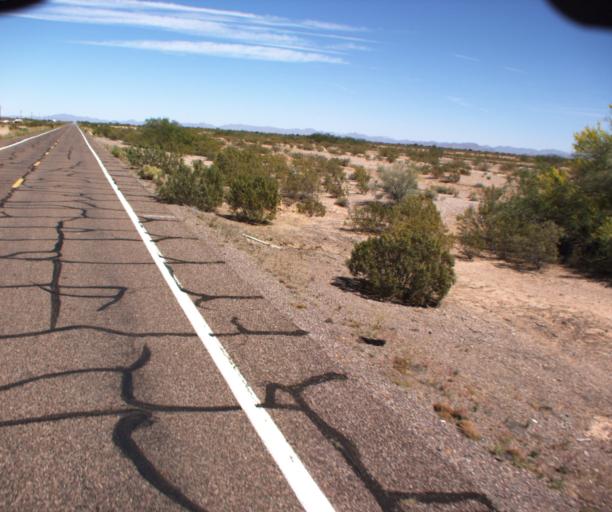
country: US
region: Arizona
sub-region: Maricopa County
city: Gila Bend
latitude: 32.8142
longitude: -112.7916
